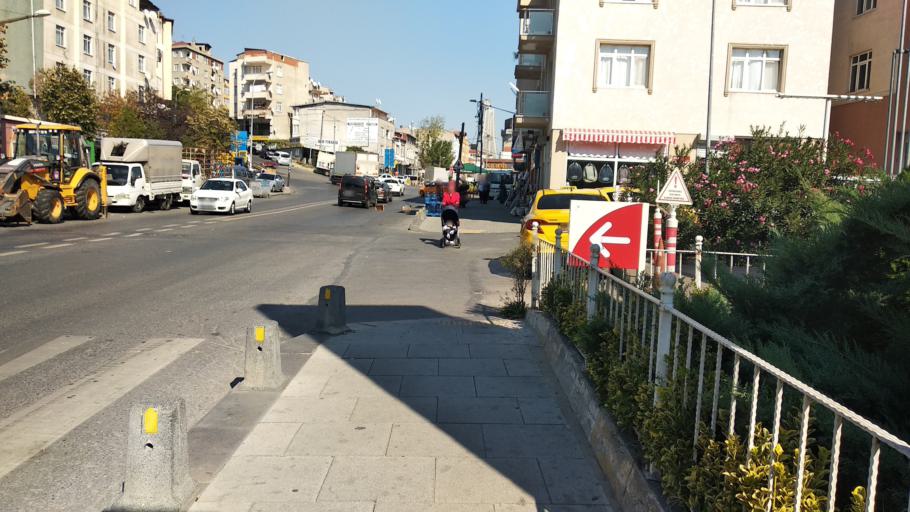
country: TR
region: Istanbul
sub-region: Atasehir
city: Atasehir
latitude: 40.9971
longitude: 29.0888
